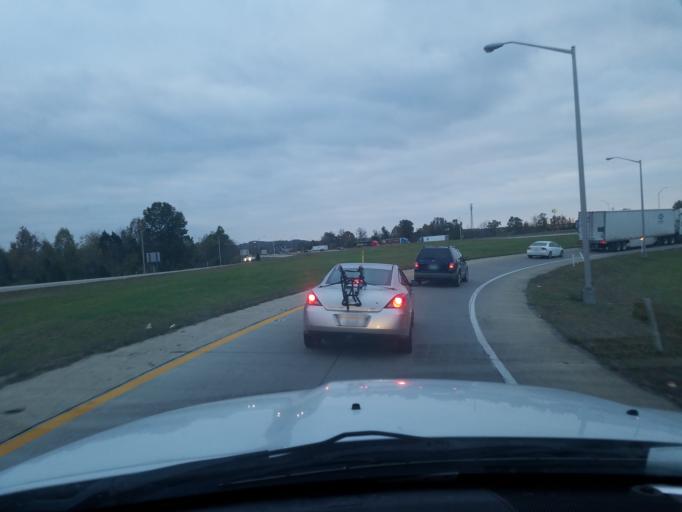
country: US
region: Kentucky
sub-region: Bullitt County
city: Shepherdsville
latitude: 37.9927
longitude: -85.7026
